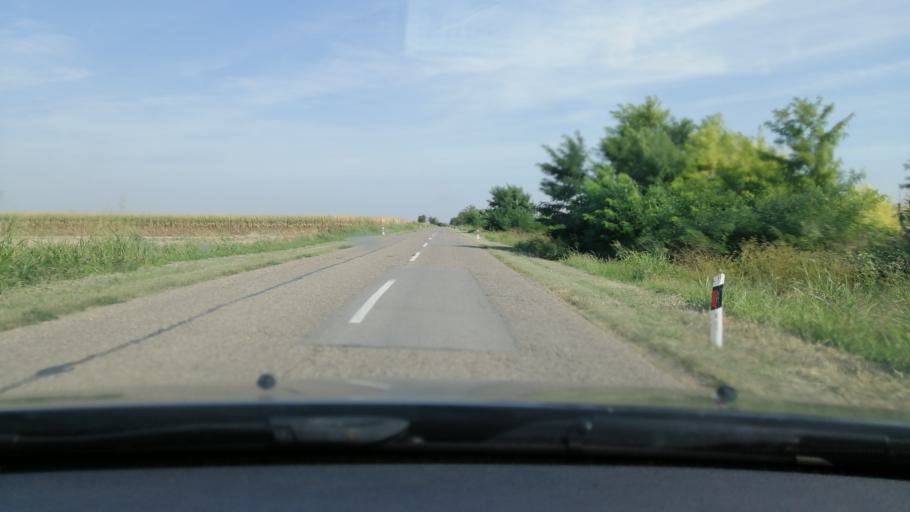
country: RS
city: Uzdin
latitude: 45.1664
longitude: 20.6174
